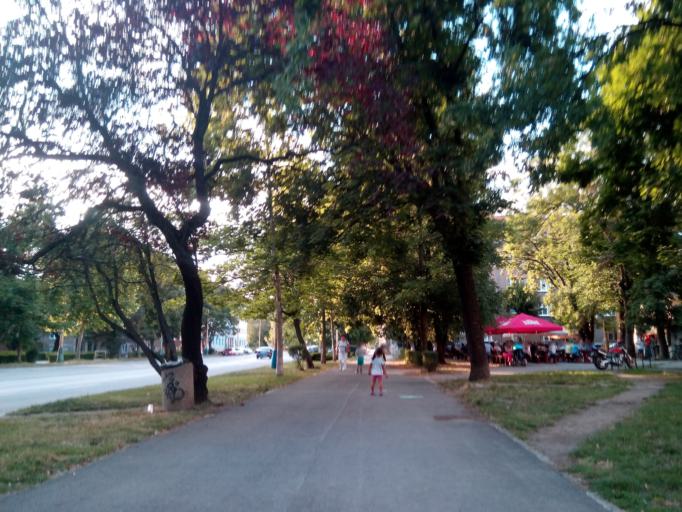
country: SK
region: Kosicky
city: Kosice
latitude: 48.7331
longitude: 21.2491
